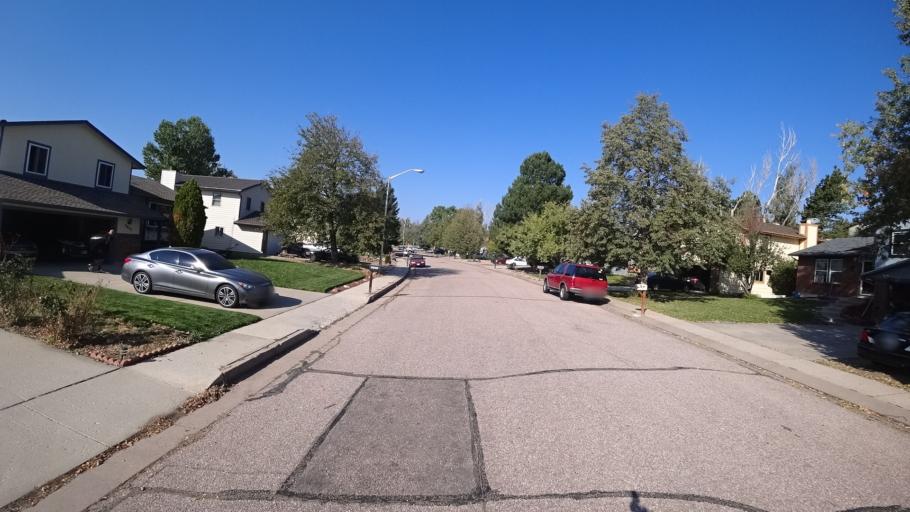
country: US
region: Colorado
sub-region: El Paso County
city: Cimarron Hills
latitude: 38.8833
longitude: -104.7232
